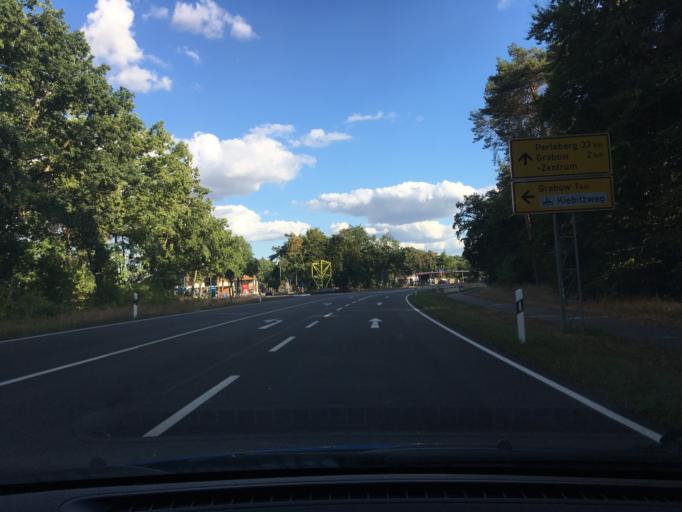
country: DE
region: Mecklenburg-Vorpommern
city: Grabow
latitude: 53.2869
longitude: 11.5518
